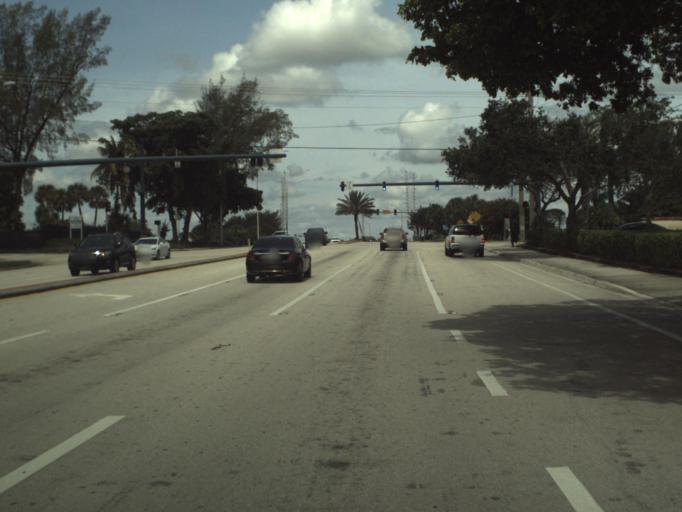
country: US
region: Florida
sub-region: Palm Beach County
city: North Palm Beach
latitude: 26.8444
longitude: -80.0636
